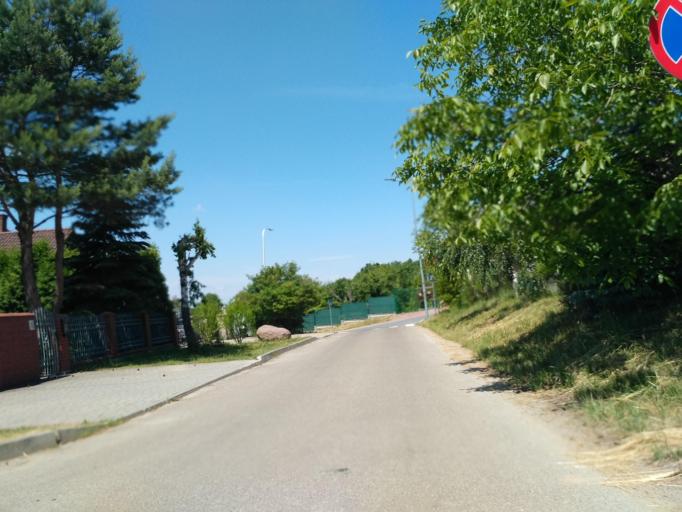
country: PL
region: Subcarpathian Voivodeship
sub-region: Krosno
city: Krosno
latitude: 49.7051
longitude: 21.7699
